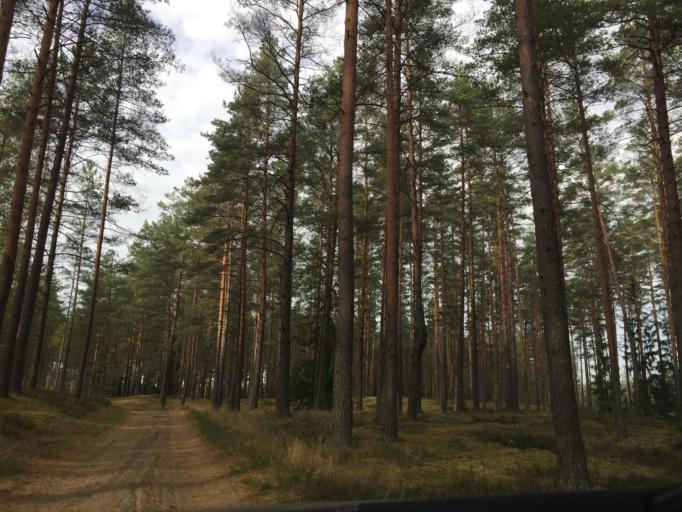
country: LV
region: Garkalne
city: Garkalne
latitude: 56.9520
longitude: 24.4261
